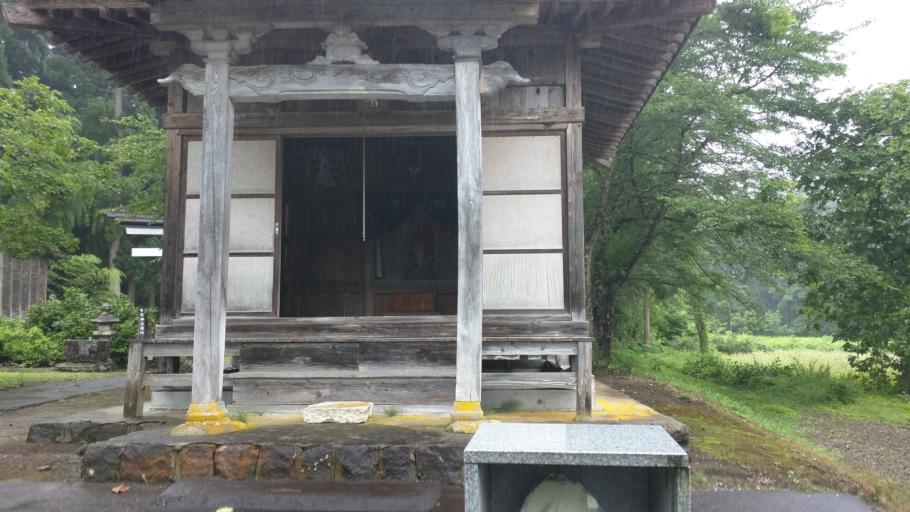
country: JP
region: Fukushima
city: Kitakata
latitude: 37.4701
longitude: 139.6530
